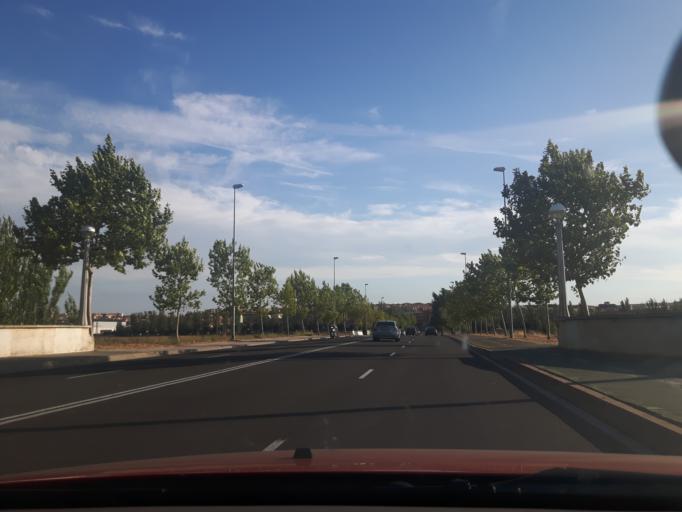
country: ES
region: Castille and Leon
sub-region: Provincia de Salamanca
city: Salamanca
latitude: 40.9616
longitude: -5.6812
